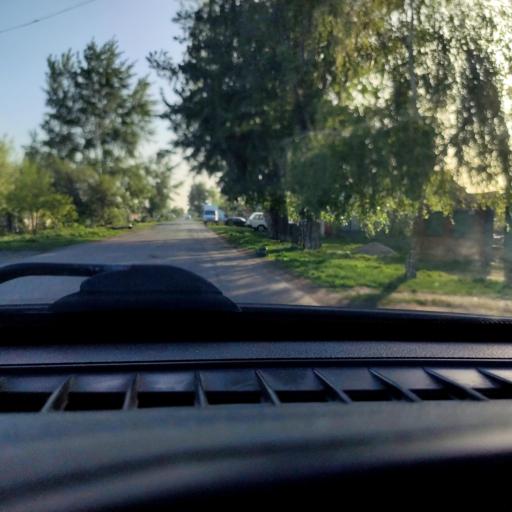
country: RU
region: Samara
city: Tol'yatti
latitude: 53.6479
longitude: 49.3115
